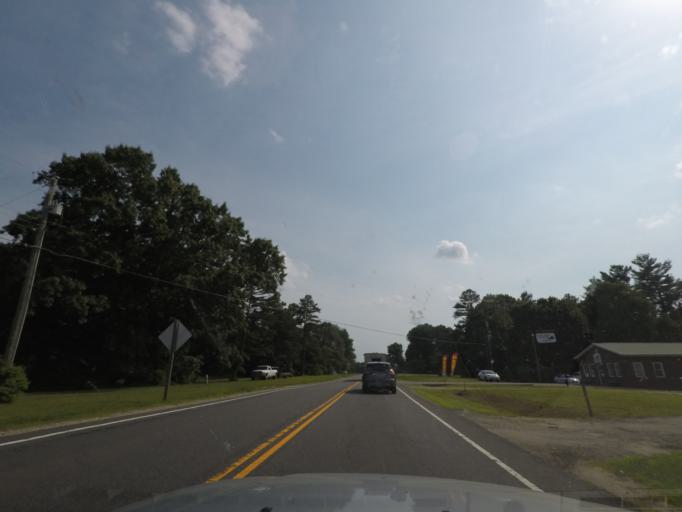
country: US
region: Virginia
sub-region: Buckingham County
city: Buckingham
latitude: 37.5241
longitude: -78.4928
